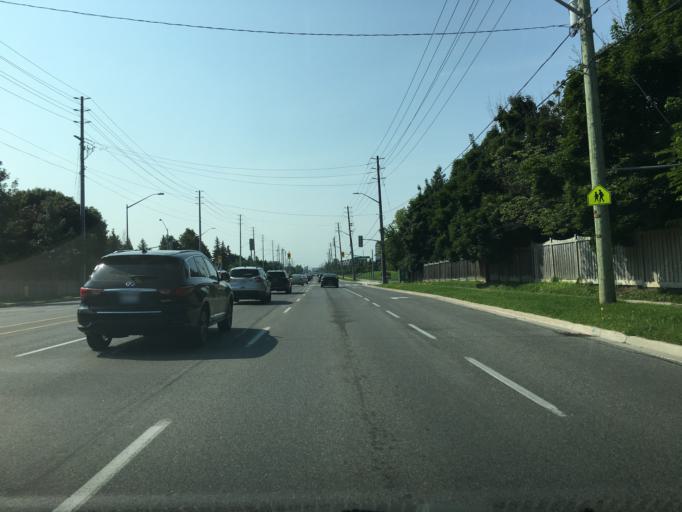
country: CA
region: Ontario
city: Markham
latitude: 43.8609
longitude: -79.3353
